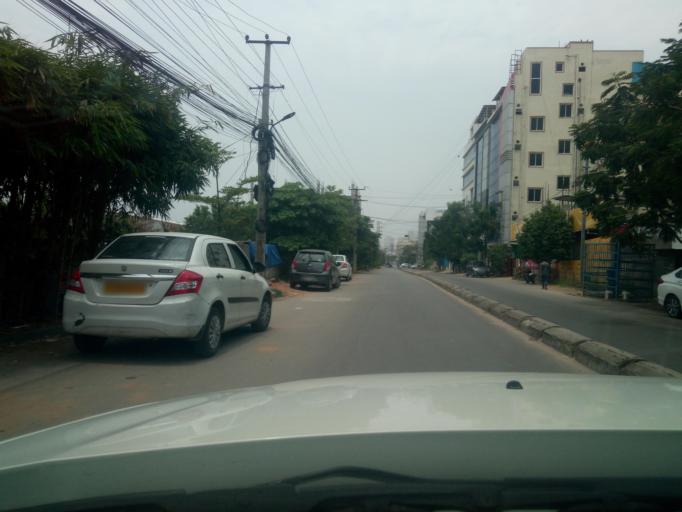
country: IN
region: Telangana
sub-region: Rangareddi
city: Kukatpalli
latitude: 17.4500
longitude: 78.3868
